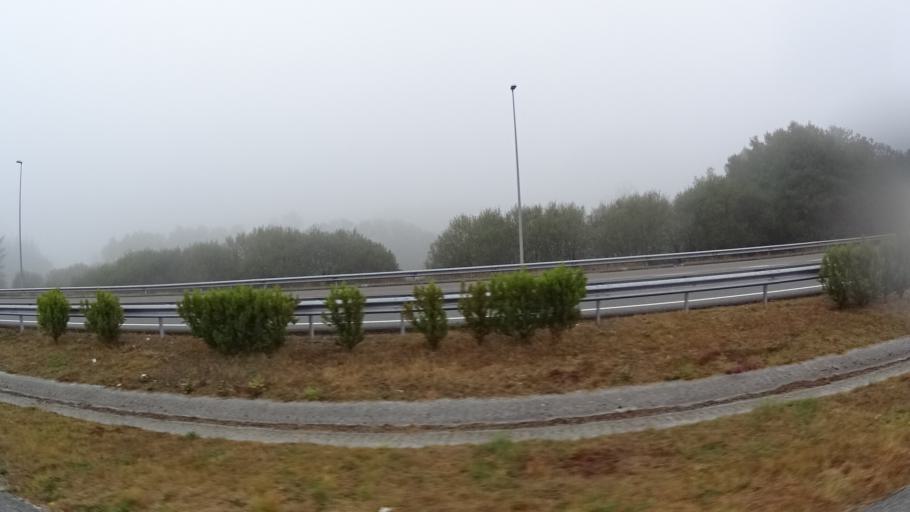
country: ES
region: Galicia
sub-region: Provincia de Lugo
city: Corgo
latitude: 42.9641
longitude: -7.4534
